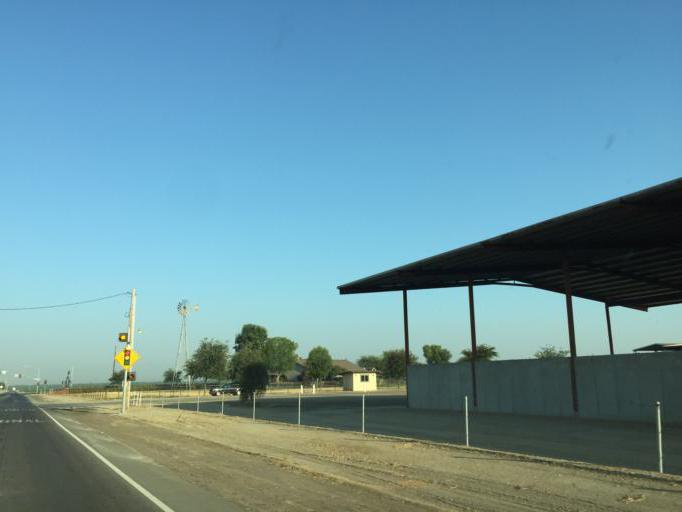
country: US
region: California
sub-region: Tulare County
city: London
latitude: 36.4585
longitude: -119.3917
